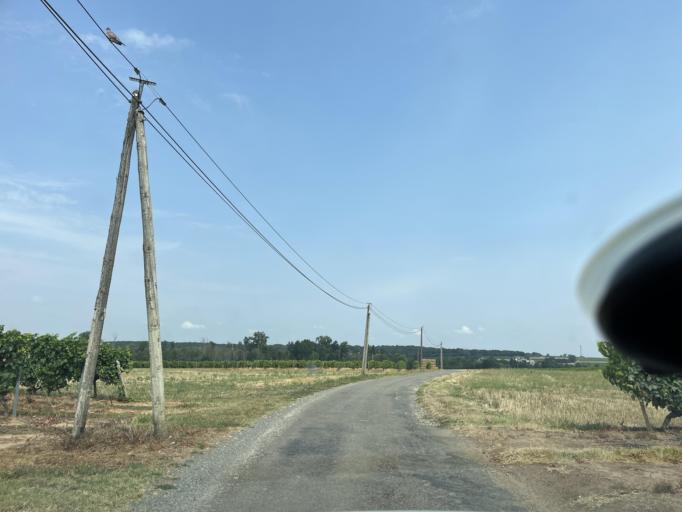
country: FR
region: Poitou-Charentes
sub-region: Departement de la Charente-Maritime
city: Pons
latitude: 45.5838
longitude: -0.5859
